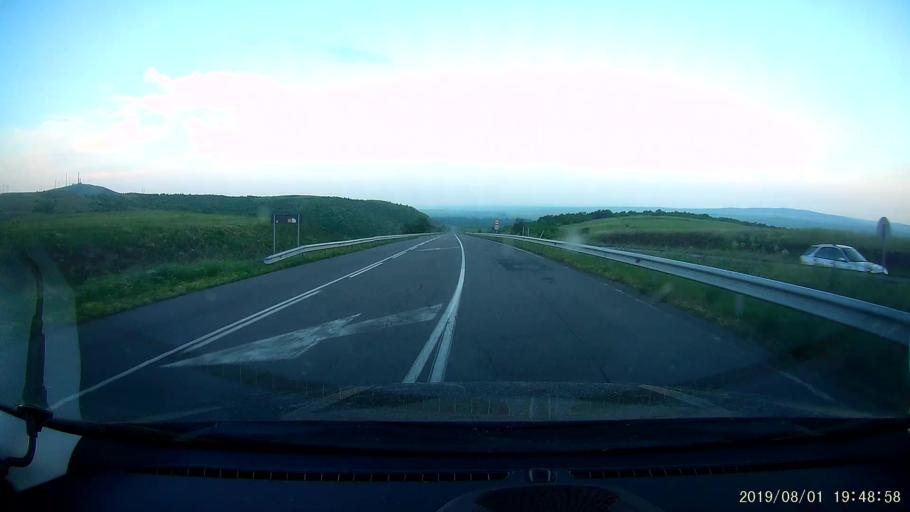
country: BG
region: Burgas
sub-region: Obshtina Karnobat
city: Karnobat
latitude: 42.6293
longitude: 26.9430
